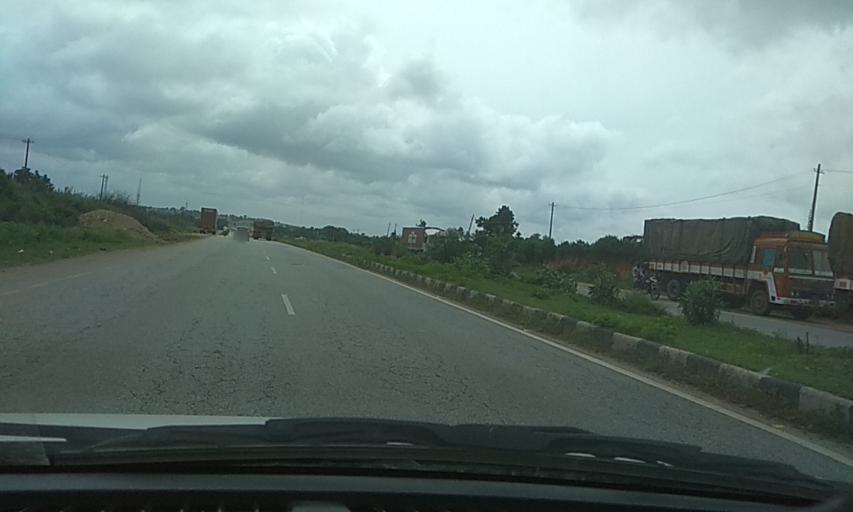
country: IN
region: Karnataka
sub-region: Davanagere
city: Mayakonda
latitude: 14.3669
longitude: 76.1507
